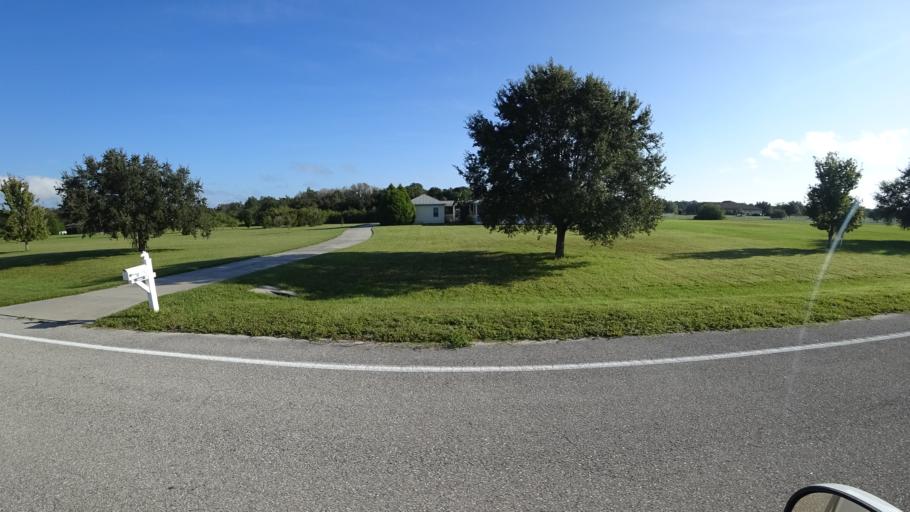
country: US
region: Florida
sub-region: Hillsborough County
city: Sun City Center
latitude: 27.5581
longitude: -82.3568
